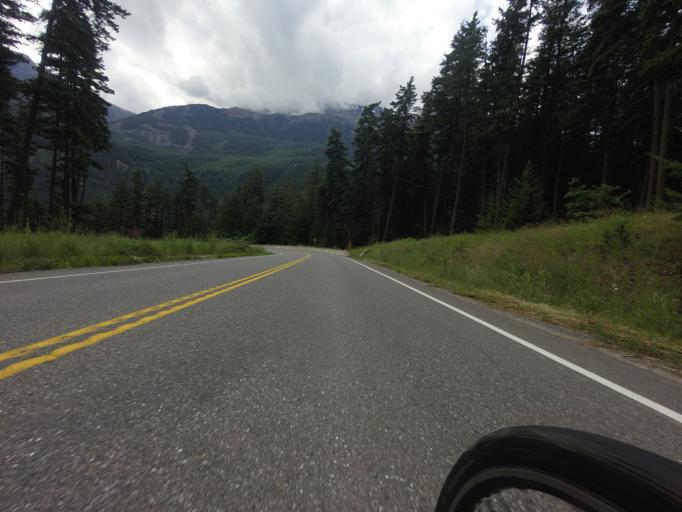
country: CA
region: British Columbia
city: Lillooet
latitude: 50.6526
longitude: -122.0103
